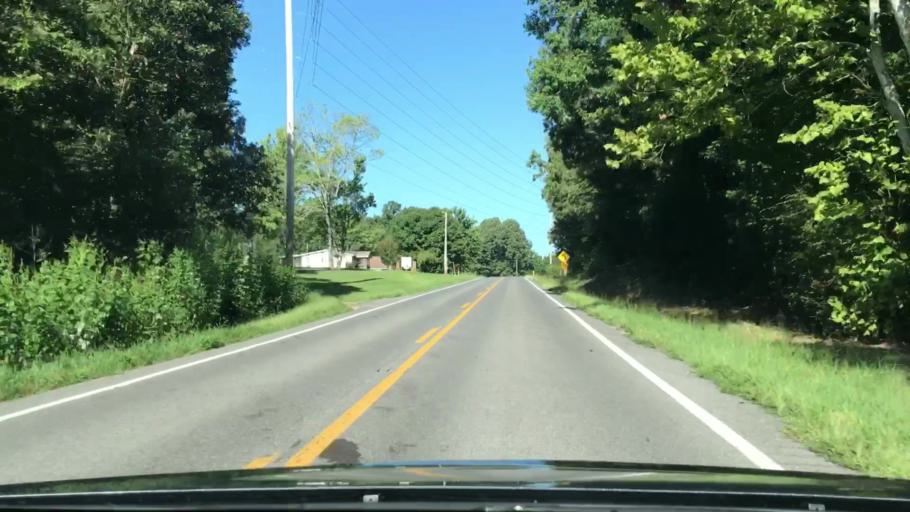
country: US
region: Kentucky
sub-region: Graves County
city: Mayfield
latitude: 36.7750
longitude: -88.4874
